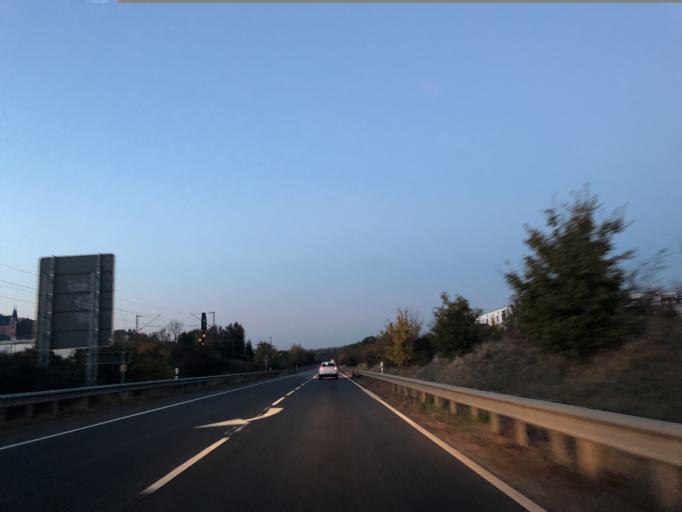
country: DE
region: Rheinland-Pfalz
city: Oppenheim
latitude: 49.8465
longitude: 8.3586
